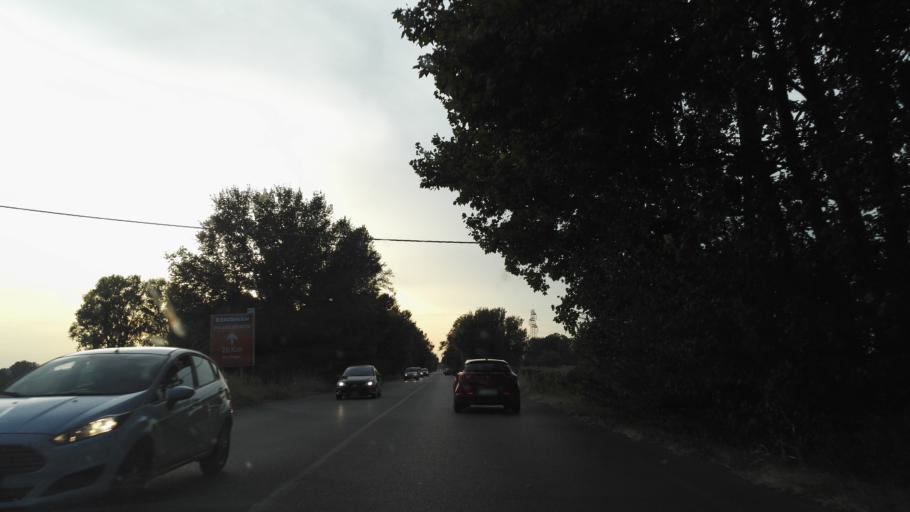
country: IT
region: Lombardy
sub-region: Citta metropolitana di Milano
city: Paullo
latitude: 45.4242
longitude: 9.4078
